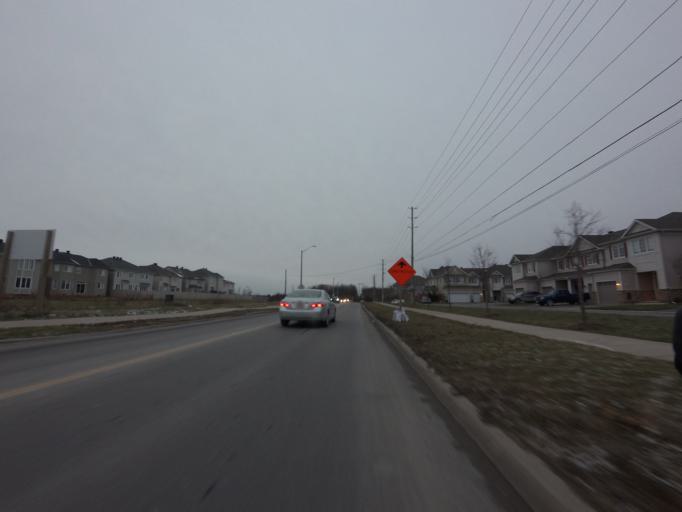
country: CA
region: Ontario
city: Bells Corners
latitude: 45.2544
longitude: -75.7367
